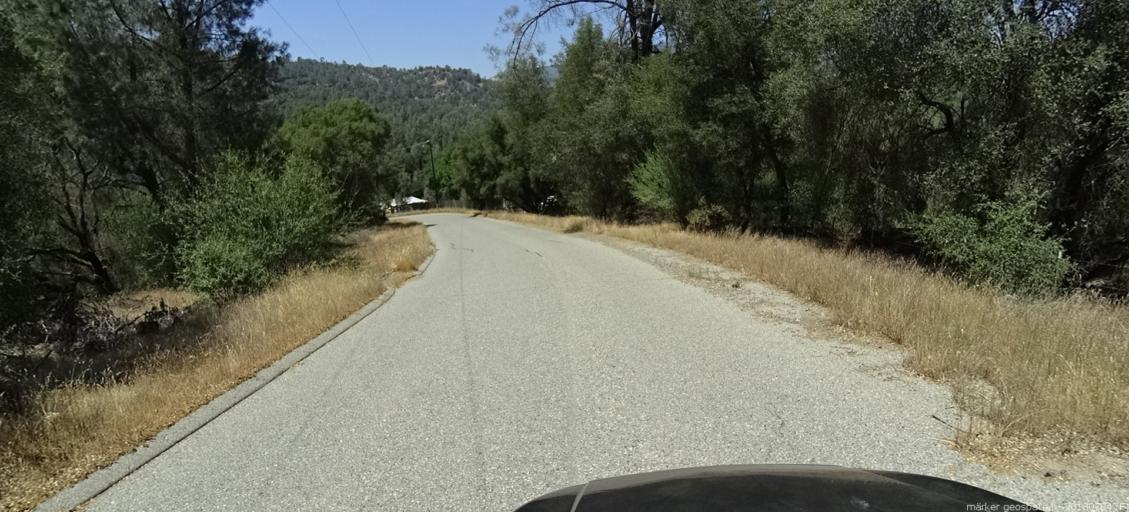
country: US
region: California
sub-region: Madera County
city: Coarsegold
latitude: 37.1855
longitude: -119.6215
